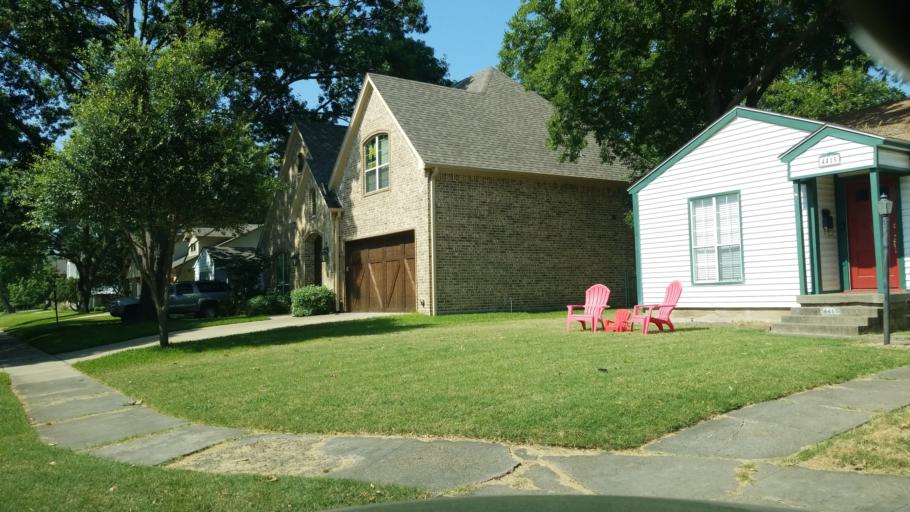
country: US
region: Texas
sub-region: Dallas County
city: Highland Park
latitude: 32.8408
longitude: -96.7645
